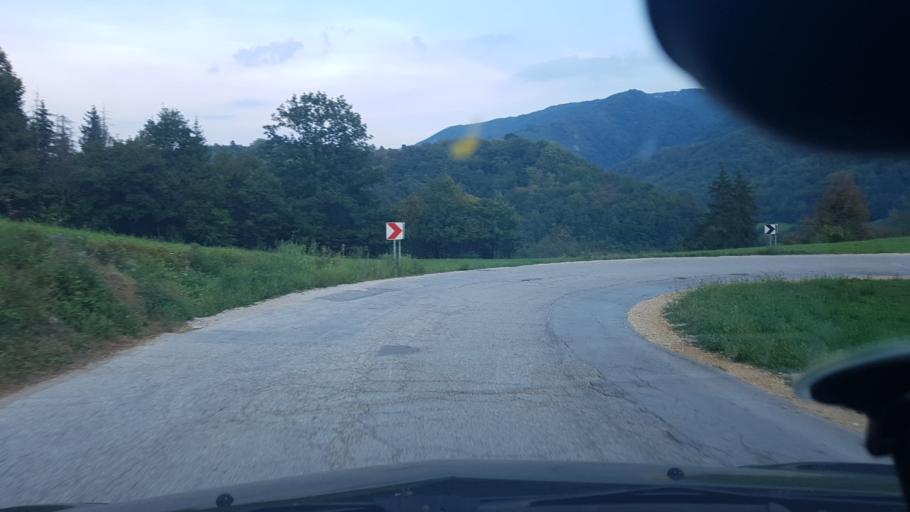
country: SI
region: Kozje
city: Kozje
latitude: 46.0406
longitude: 15.5876
